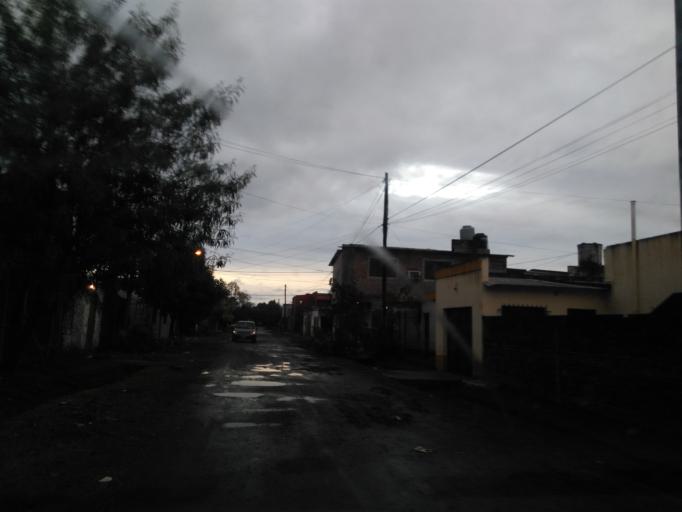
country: AR
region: Chaco
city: Resistencia
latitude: -27.4687
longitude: -58.9788
